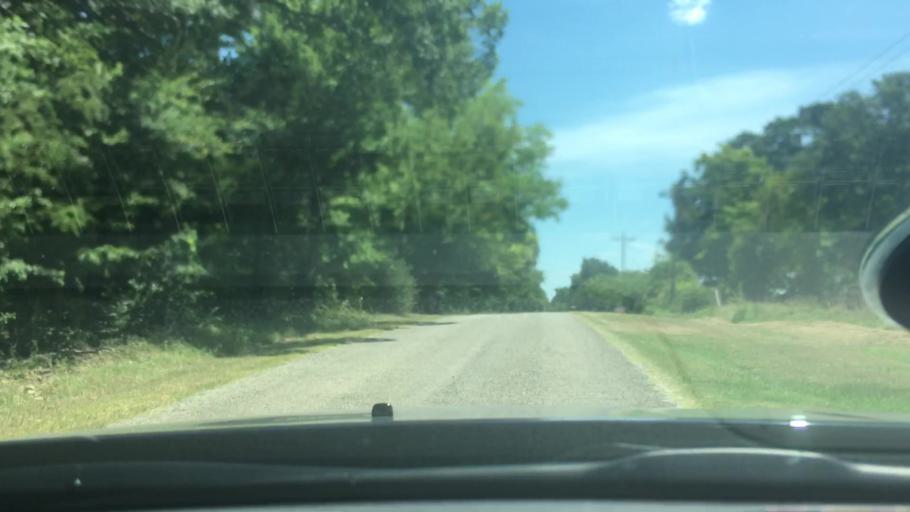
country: US
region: Oklahoma
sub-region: Bryan County
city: Durant
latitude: 33.9830
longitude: -96.2412
